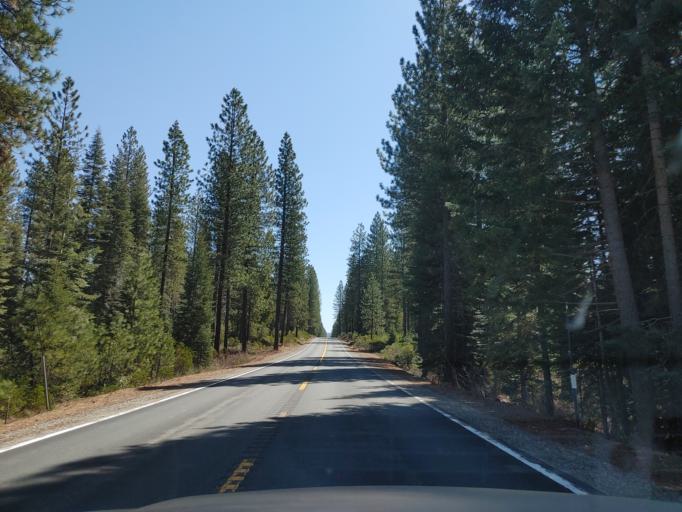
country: US
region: California
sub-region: Siskiyou County
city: McCloud
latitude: 41.2626
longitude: -121.8479
